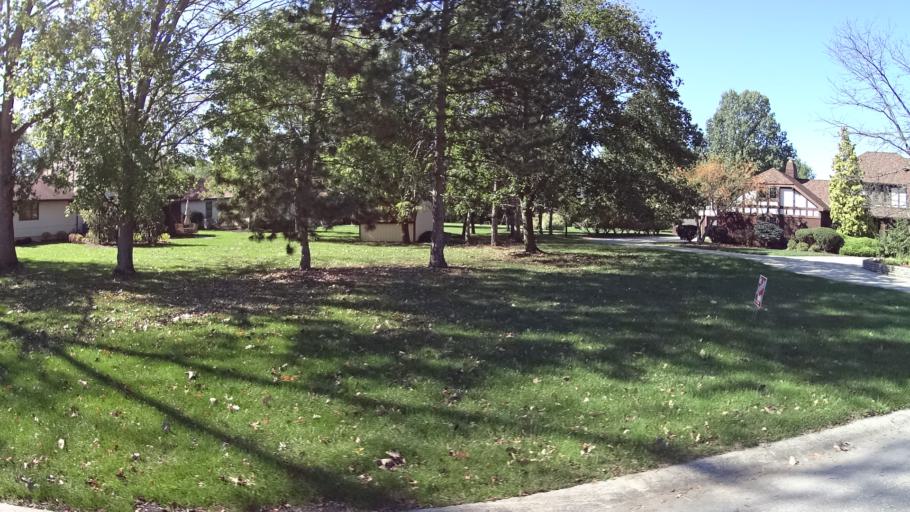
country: US
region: Ohio
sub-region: Lorain County
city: Amherst
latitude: 41.4119
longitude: -82.2201
